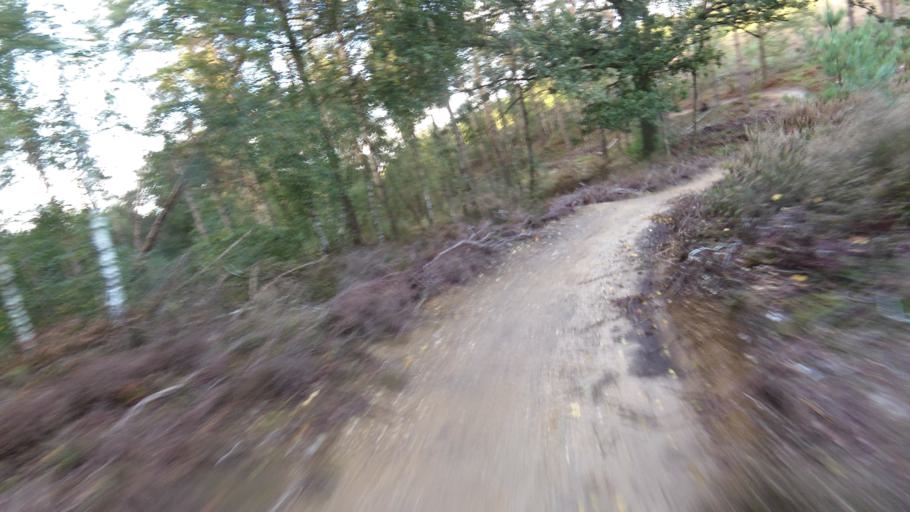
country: NL
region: Utrecht
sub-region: Gemeente Utrechtse Heuvelrug
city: Overberg
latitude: 52.0031
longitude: 5.5063
